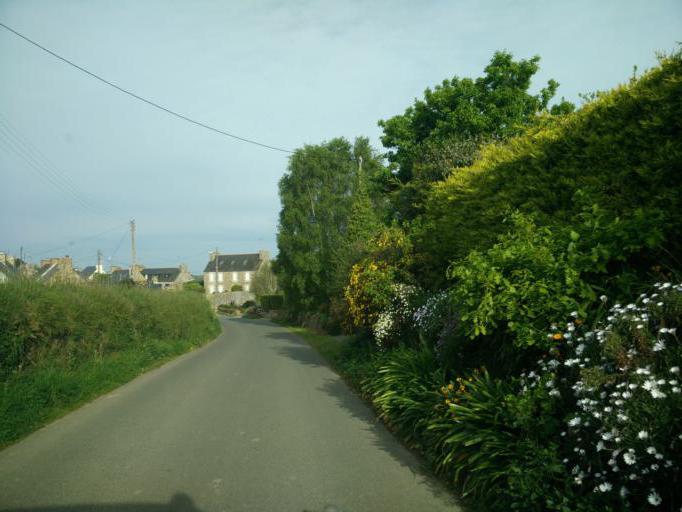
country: FR
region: Brittany
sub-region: Departement des Cotes-d'Armor
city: Lezardrieux
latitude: 48.8268
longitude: -3.0906
